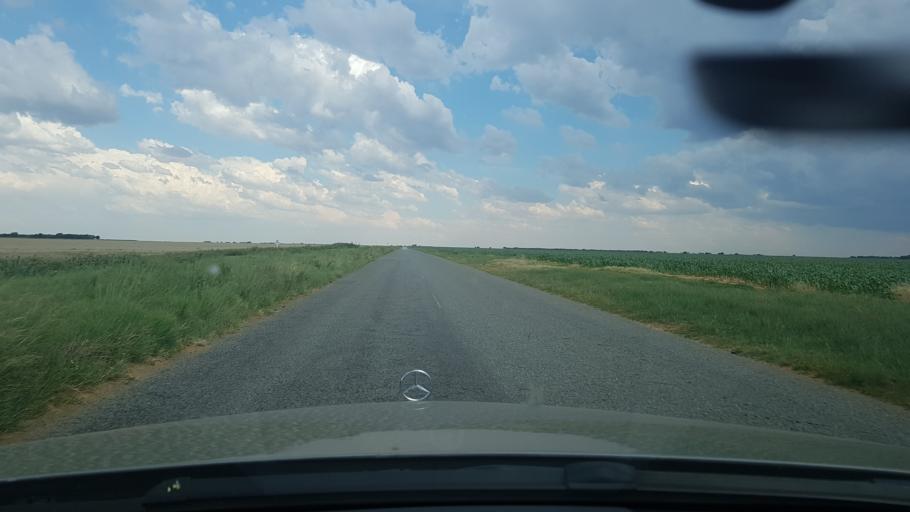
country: ZA
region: North-West
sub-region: Dr Ruth Segomotsi Mompati District Municipality
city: Bloemhof
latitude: -27.8838
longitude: 25.6656
